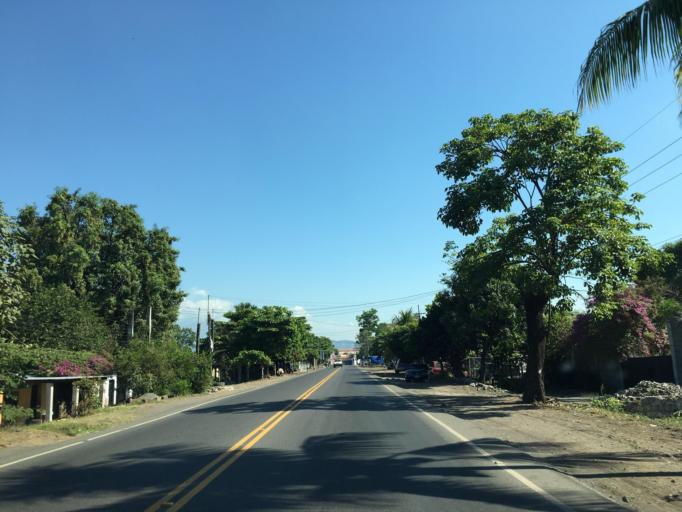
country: GT
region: Escuintla
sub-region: Municipio de La Democracia
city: La Democracia
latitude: 14.2244
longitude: -90.9498
